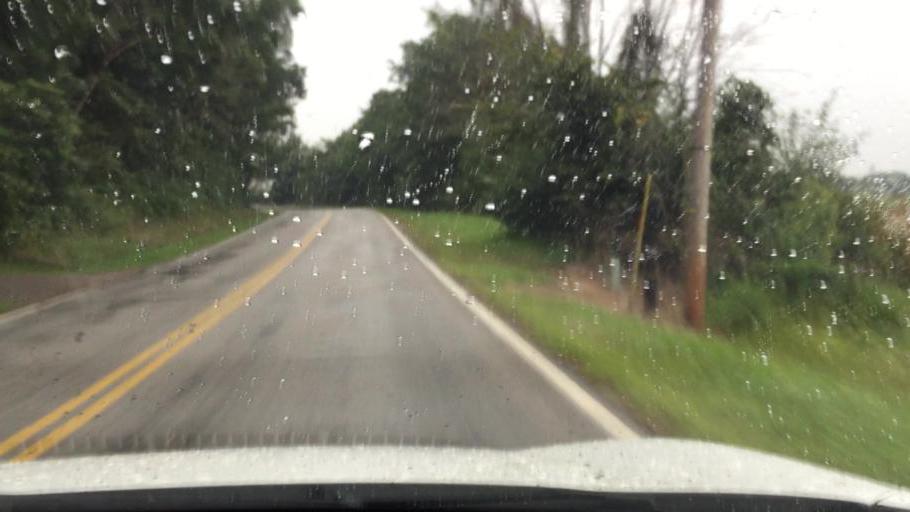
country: US
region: Ohio
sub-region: Clark County
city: Northridge
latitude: 39.9877
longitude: -83.6665
